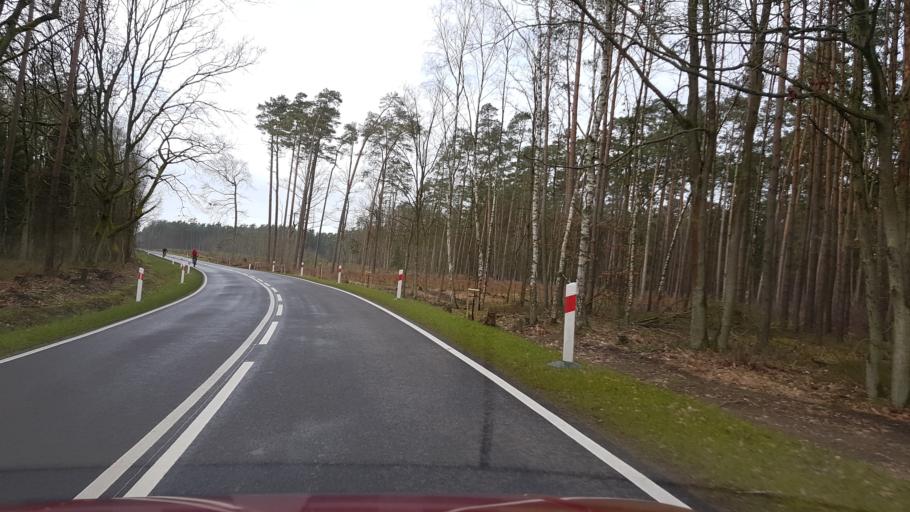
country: PL
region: West Pomeranian Voivodeship
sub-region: Powiat policki
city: Police
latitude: 53.6643
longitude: 14.4597
